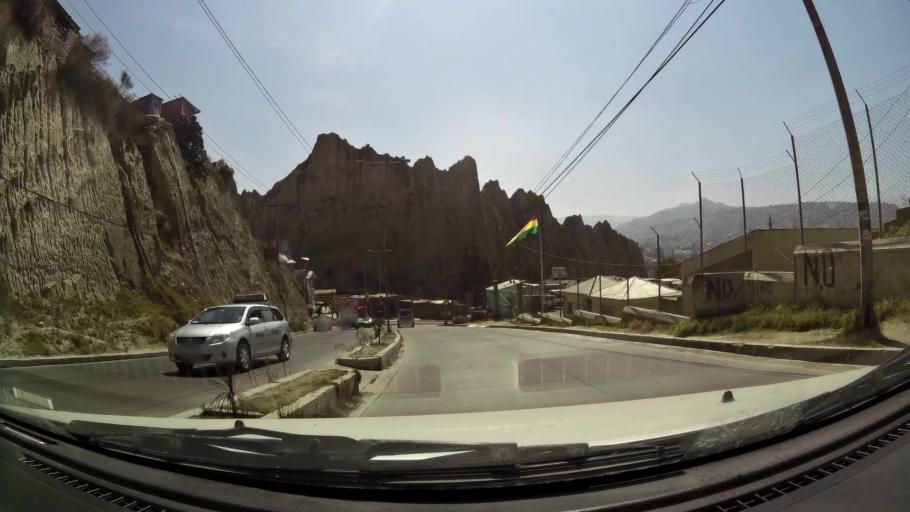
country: BO
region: La Paz
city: La Paz
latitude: -16.5256
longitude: -68.1237
